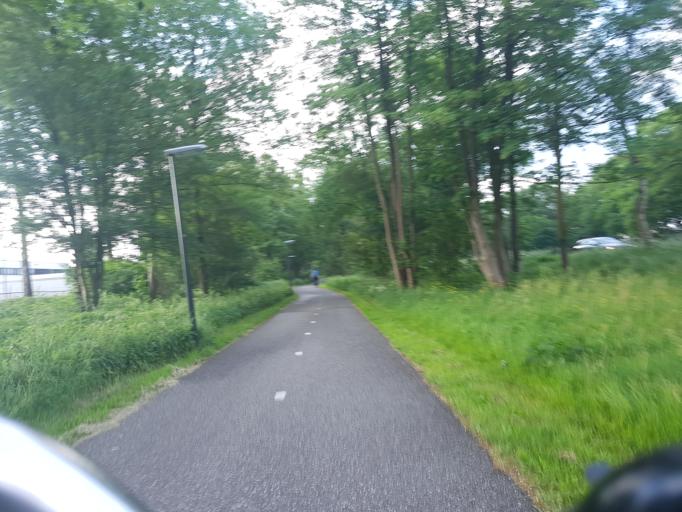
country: NL
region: Gelderland
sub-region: Gemeente Apeldoorn
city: Apeldoorn
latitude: 52.1881
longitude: 5.9880
